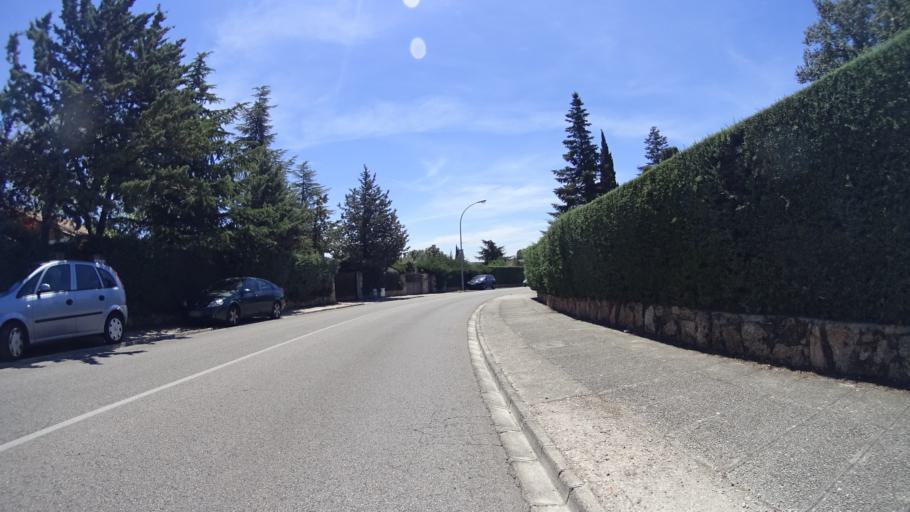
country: ES
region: Madrid
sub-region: Provincia de Madrid
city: Hoyo de Manzanares
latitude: 40.6114
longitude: -3.9358
